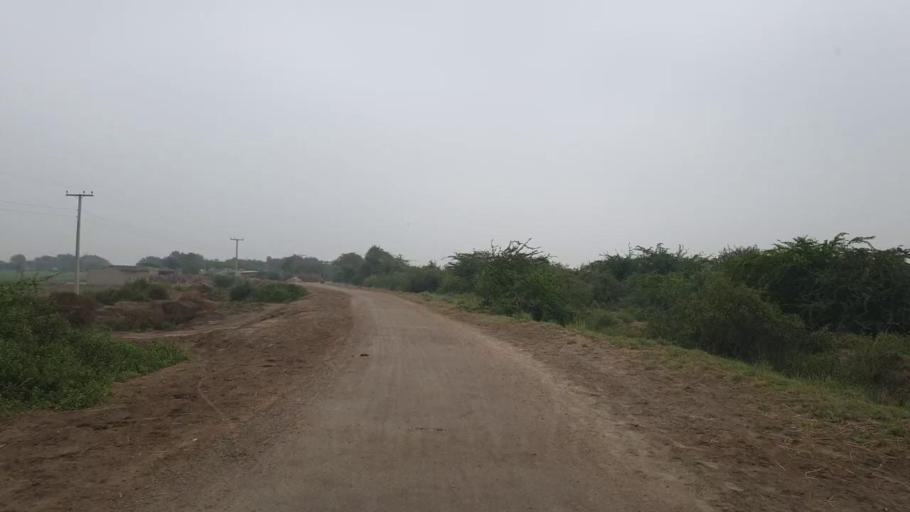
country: PK
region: Sindh
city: Badin
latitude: 24.5981
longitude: 68.6746
